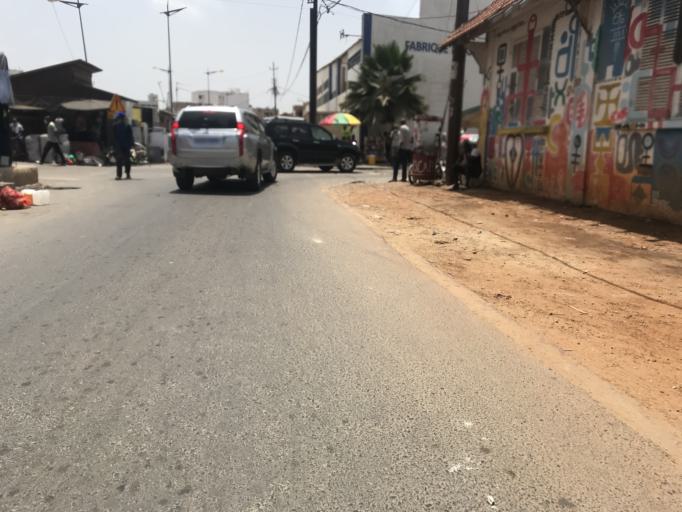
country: SN
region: Dakar
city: Dakar
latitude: 14.6785
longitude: -17.4570
